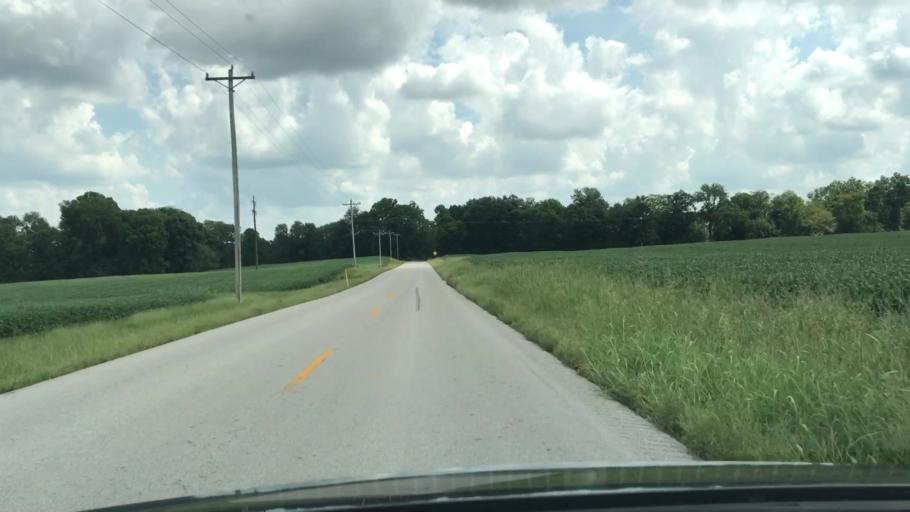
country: US
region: Kentucky
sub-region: Todd County
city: Elkton
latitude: 36.7925
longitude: -87.1439
